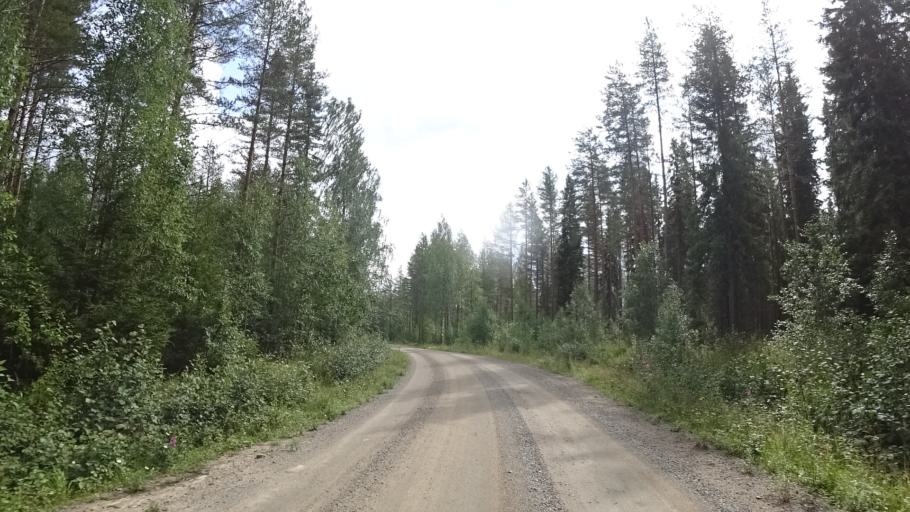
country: FI
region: North Karelia
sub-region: Joensuu
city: Ilomantsi
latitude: 62.9233
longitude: 31.3343
